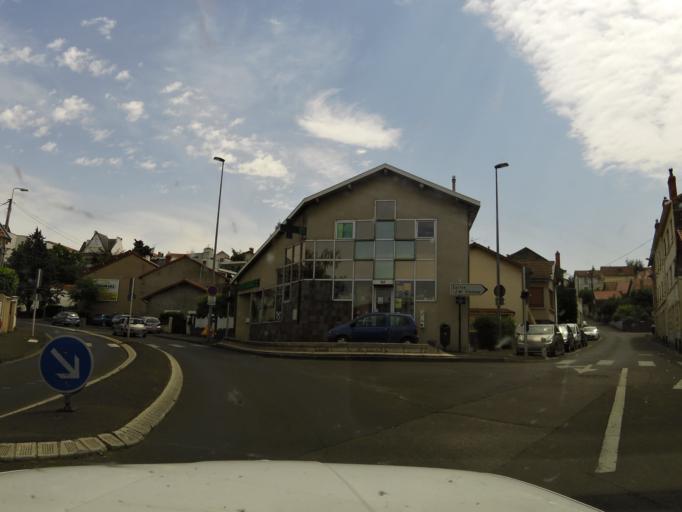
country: FR
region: Auvergne
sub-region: Departement du Puy-de-Dome
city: Beaumont
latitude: 45.7575
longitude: 3.0809
